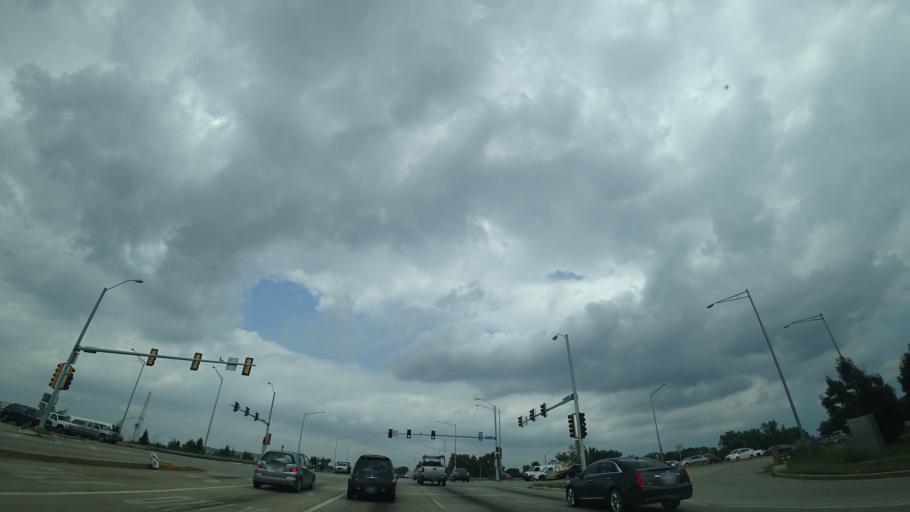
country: US
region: Illinois
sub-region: Cook County
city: Alsip
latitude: 41.6614
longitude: -87.7385
